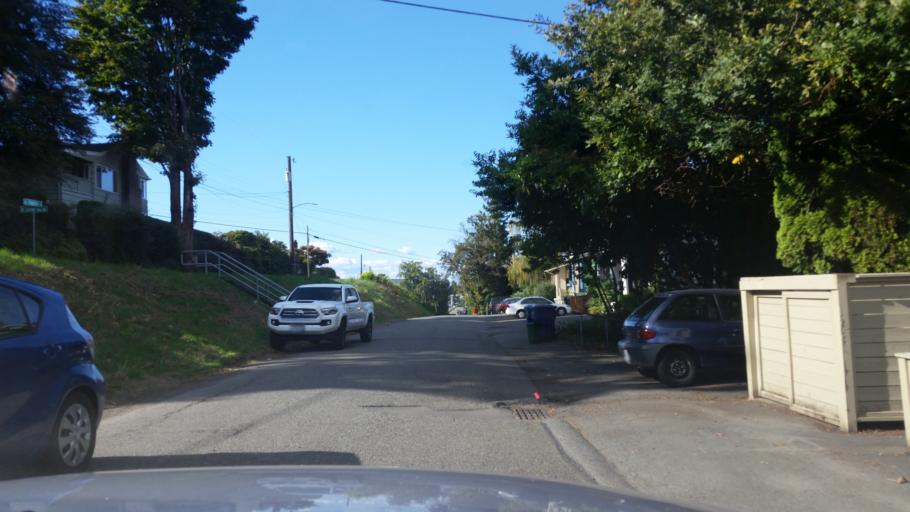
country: US
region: Washington
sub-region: King County
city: Seattle
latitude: 47.6531
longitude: -122.3707
